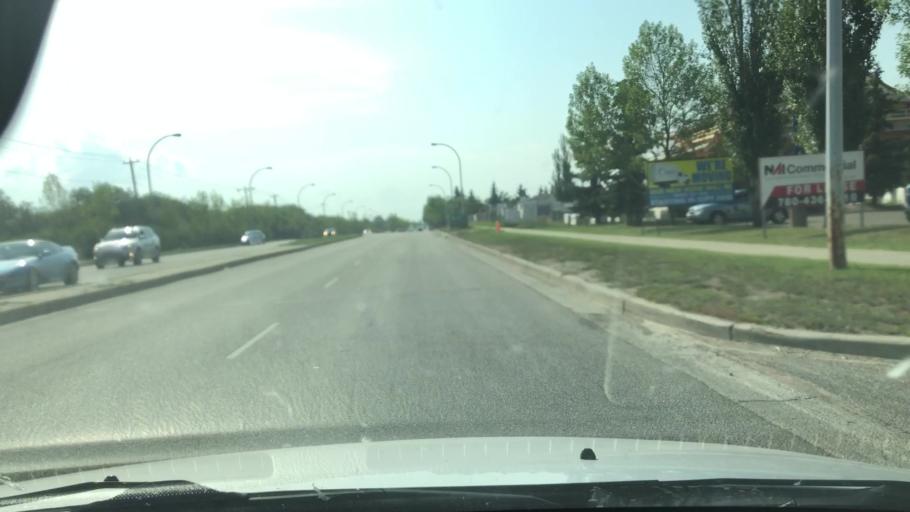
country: CA
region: Alberta
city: Edmonton
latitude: 53.6141
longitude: -113.4950
